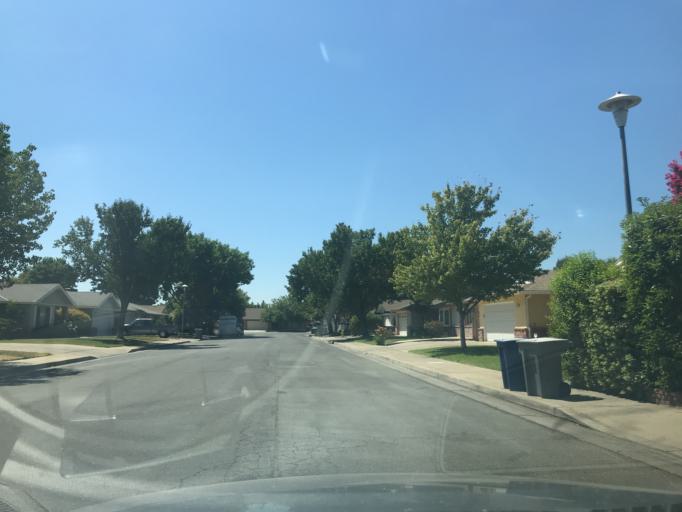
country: US
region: California
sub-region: Merced County
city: Merced
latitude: 37.3366
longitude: -120.4805
